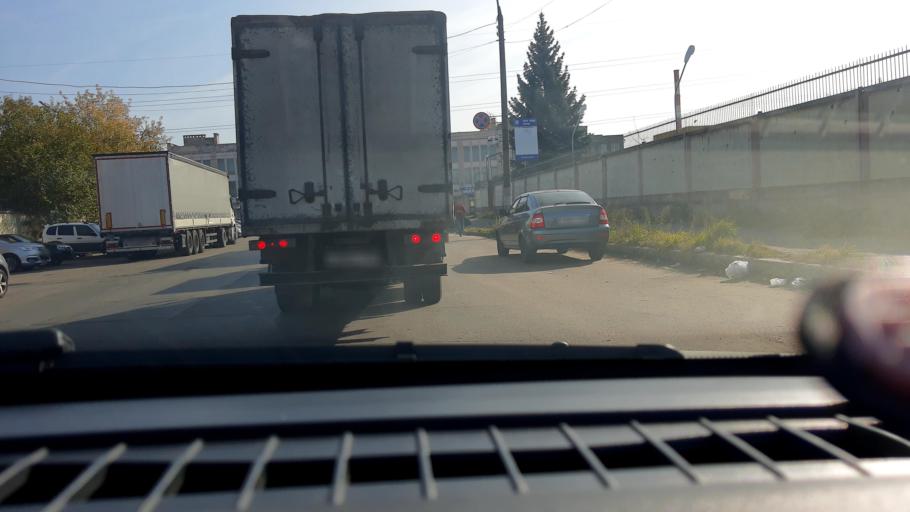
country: RU
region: Nizjnij Novgorod
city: Burevestnik
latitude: 56.2349
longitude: 43.8863
